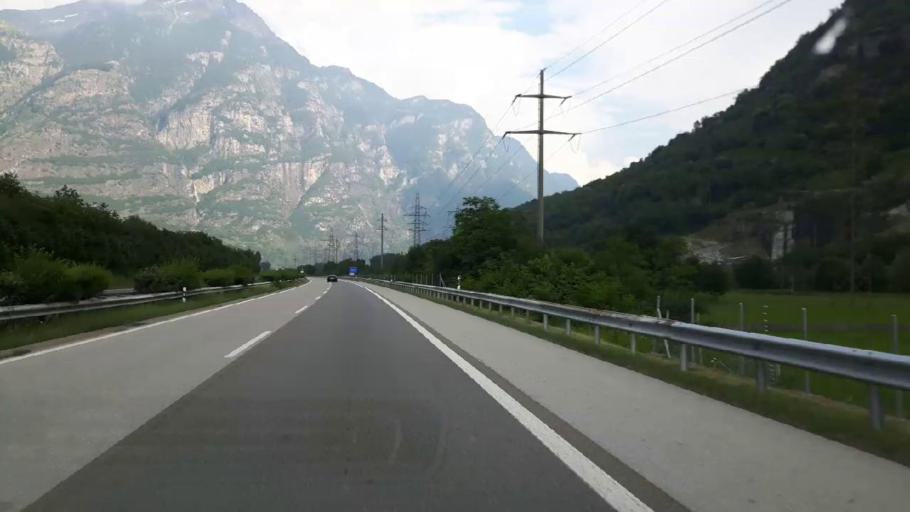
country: CH
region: Ticino
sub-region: Riviera District
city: Biasca
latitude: 46.3632
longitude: 8.9390
